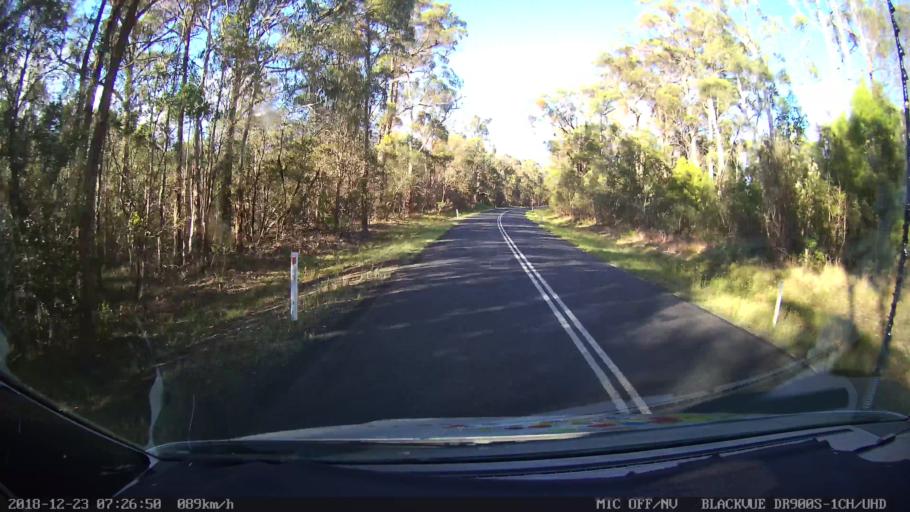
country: AU
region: New South Wales
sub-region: Armidale Dumaresq
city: Enmore
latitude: -30.4941
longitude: 152.1935
